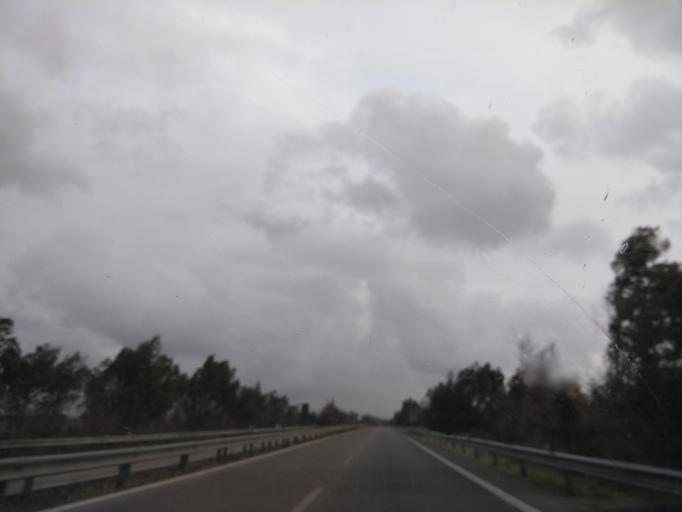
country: IT
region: Sicily
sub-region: Trapani
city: Erice
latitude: 38.0044
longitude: 12.5852
